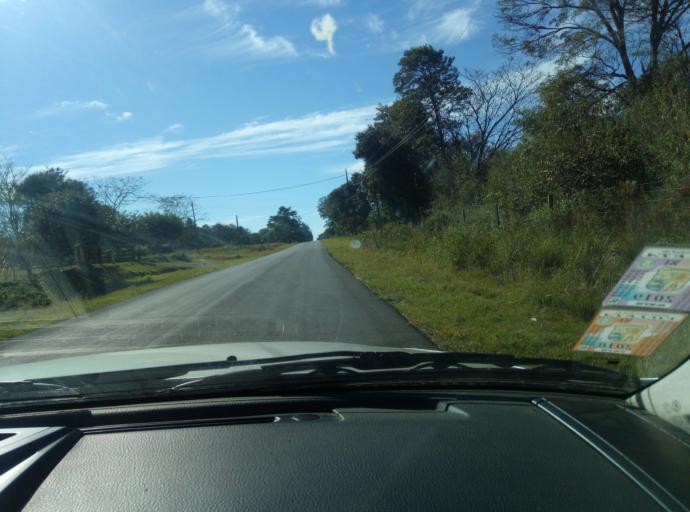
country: PY
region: Caaguazu
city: Carayao
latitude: -25.1686
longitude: -56.3131
